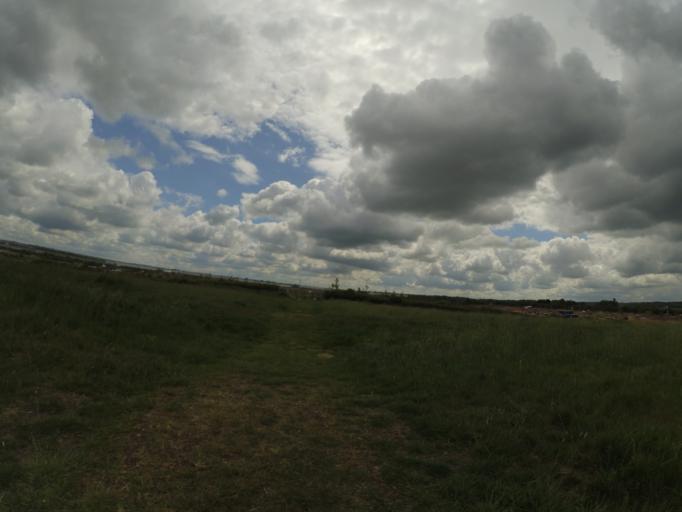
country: GB
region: England
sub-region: Warwickshire
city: Rugby
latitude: 52.3612
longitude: -1.1960
